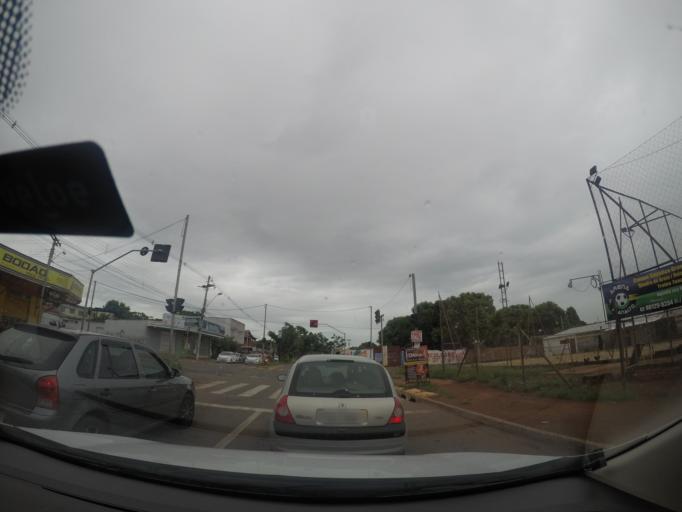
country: BR
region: Goias
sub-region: Goiania
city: Goiania
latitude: -16.6201
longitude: -49.3381
